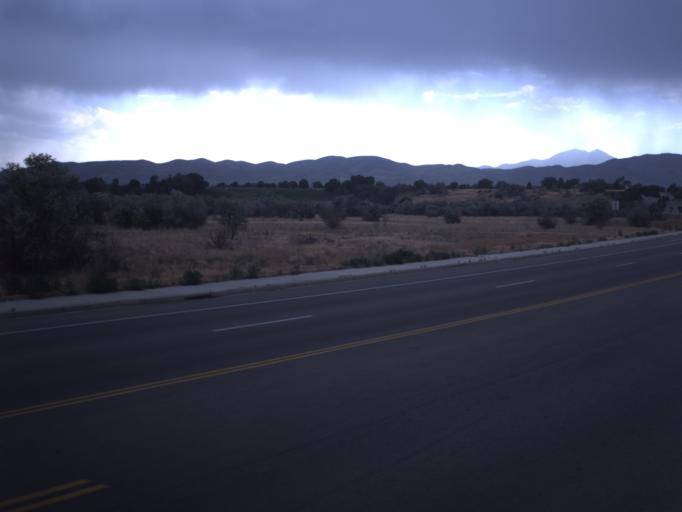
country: US
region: Utah
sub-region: Salt Lake County
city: Riverton
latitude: 40.5266
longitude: -111.9156
